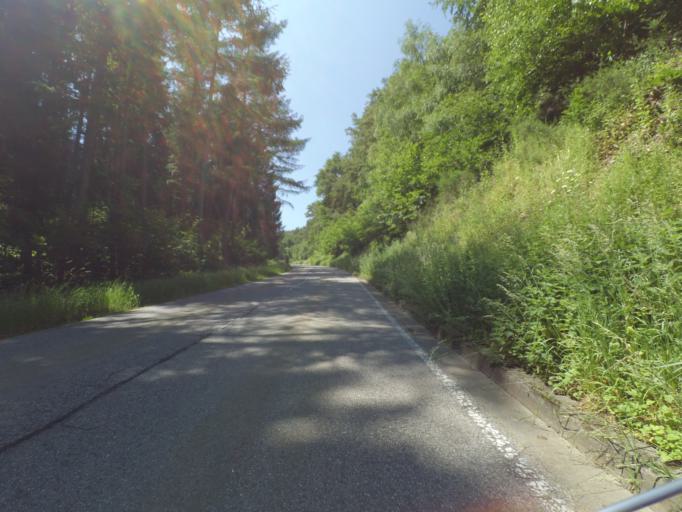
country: DE
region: Rheinland-Pfalz
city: Utzenhain
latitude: 50.1381
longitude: 7.6325
